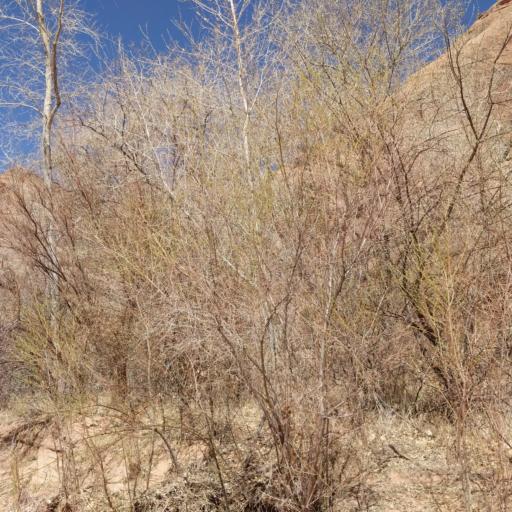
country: US
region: Arizona
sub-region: Apache County
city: Chinle
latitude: 36.1578
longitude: -109.4655
